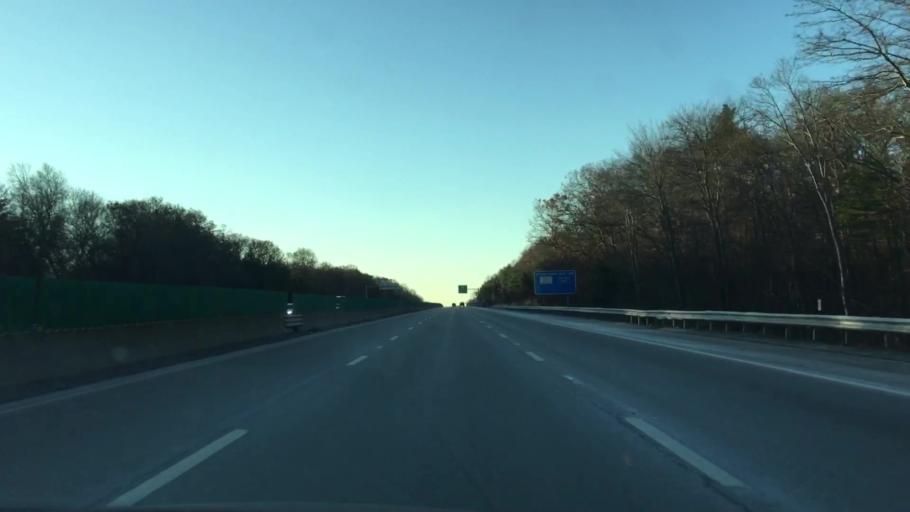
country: US
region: Massachusetts
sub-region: Norfolk County
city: Avon
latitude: 42.1154
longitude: -71.0603
